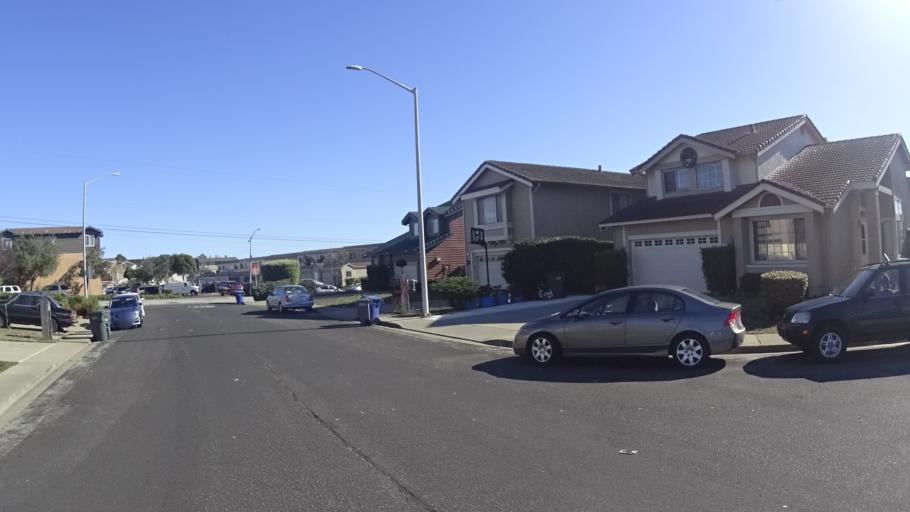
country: US
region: California
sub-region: San Mateo County
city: South San Francisco
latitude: 37.6632
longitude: -122.4329
